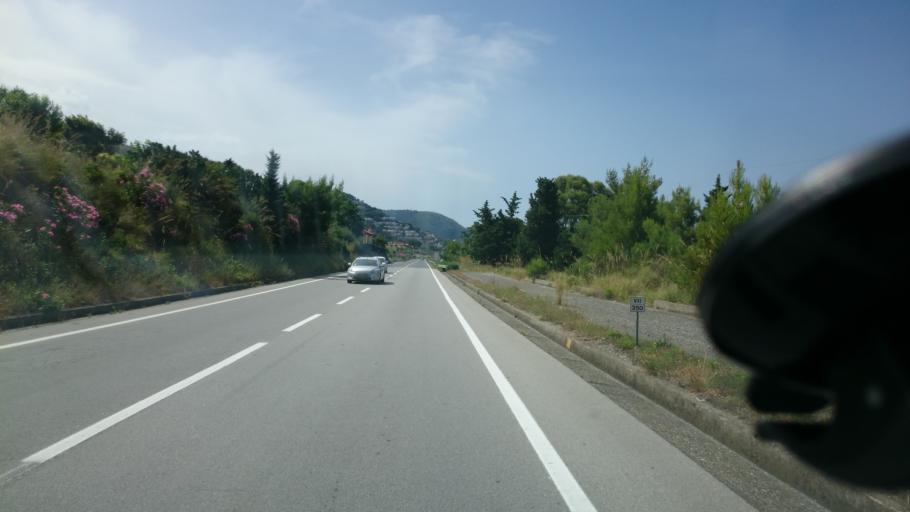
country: IT
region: Calabria
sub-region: Provincia di Cosenza
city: Praia a Mare
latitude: 39.8824
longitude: 15.7941
